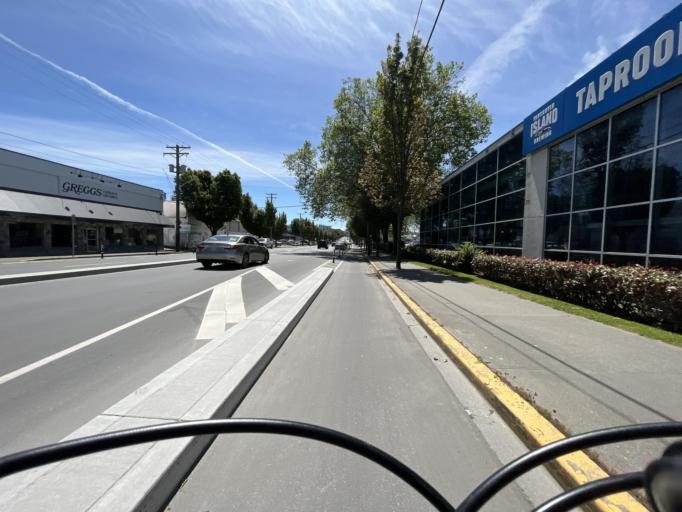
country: CA
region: British Columbia
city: Victoria
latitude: 48.4351
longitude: -123.3674
